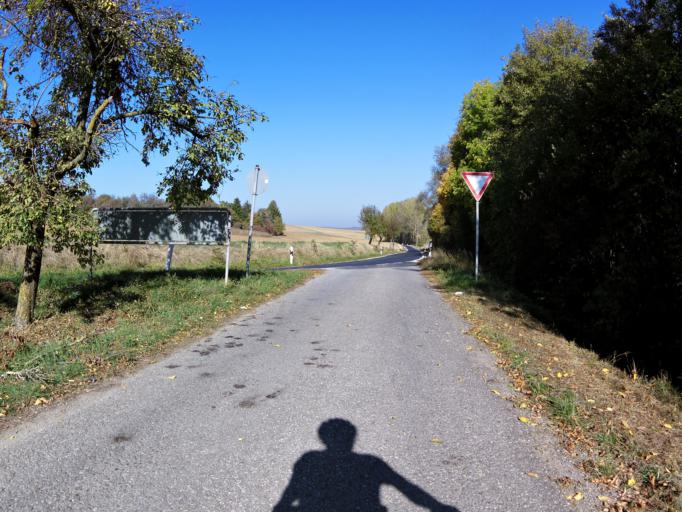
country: DE
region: Bavaria
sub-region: Regierungsbezirk Unterfranken
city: Geroldshausen
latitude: 49.7060
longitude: 9.9091
